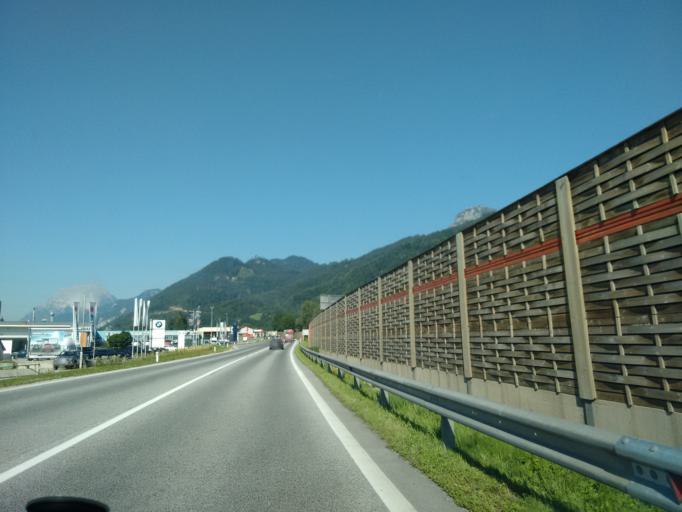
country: AT
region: Styria
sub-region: Politischer Bezirk Liezen
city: Weissenbach bei Liezen
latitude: 47.5700
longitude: 14.2159
